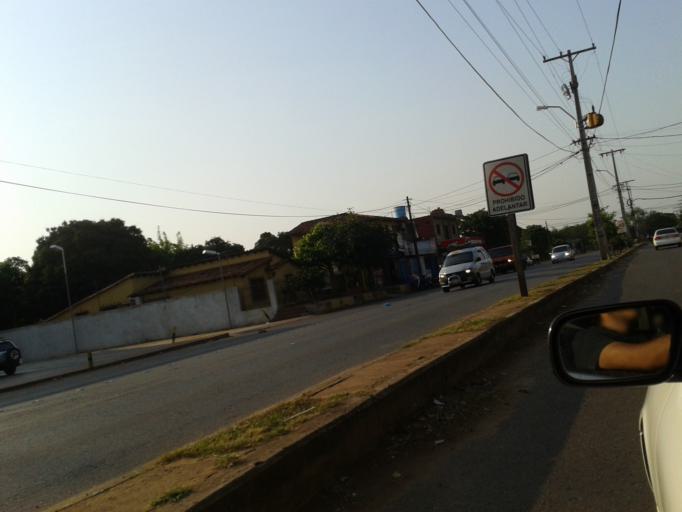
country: PY
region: Guaira
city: Villarrica
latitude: -25.7705
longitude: -56.4398
